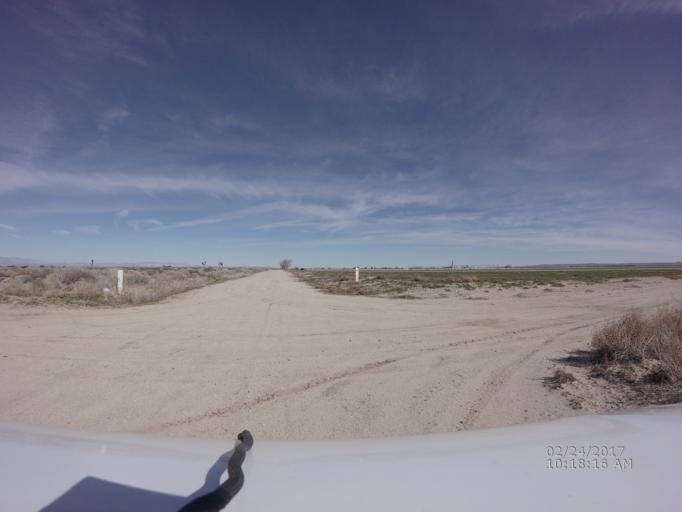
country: US
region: California
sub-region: Los Angeles County
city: Littlerock
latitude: 34.6607
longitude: -117.9874
